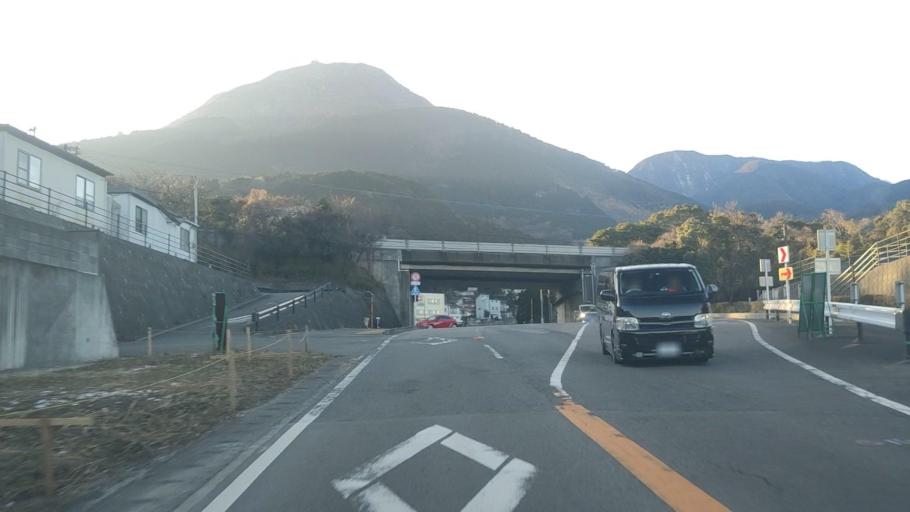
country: JP
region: Oita
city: Beppu
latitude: 33.2876
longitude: 131.4652
